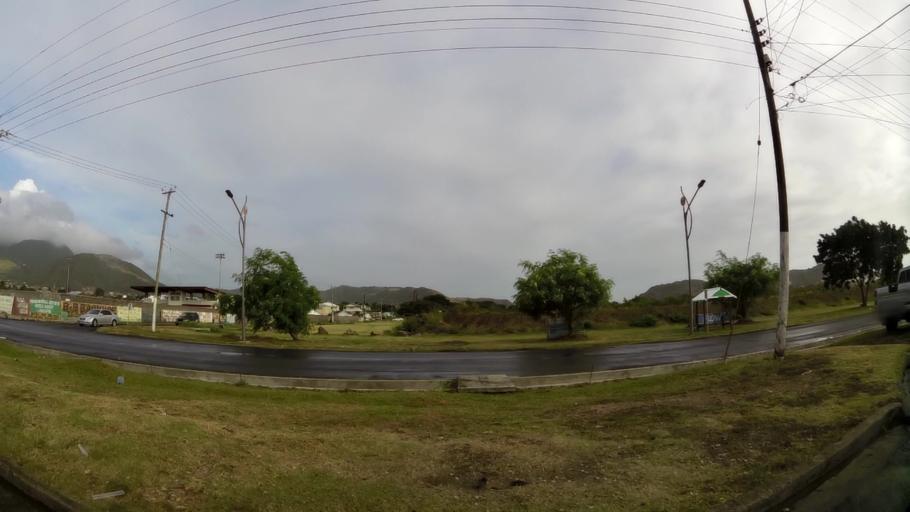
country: KN
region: Saint George Basseterre
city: Basseterre
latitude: 17.2967
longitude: -62.7156
